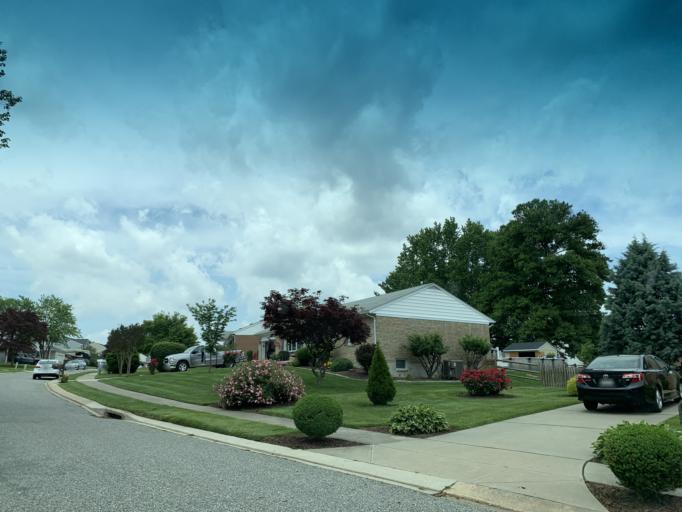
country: US
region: Maryland
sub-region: Harford County
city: South Bel Air
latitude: 39.5410
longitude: -76.3015
